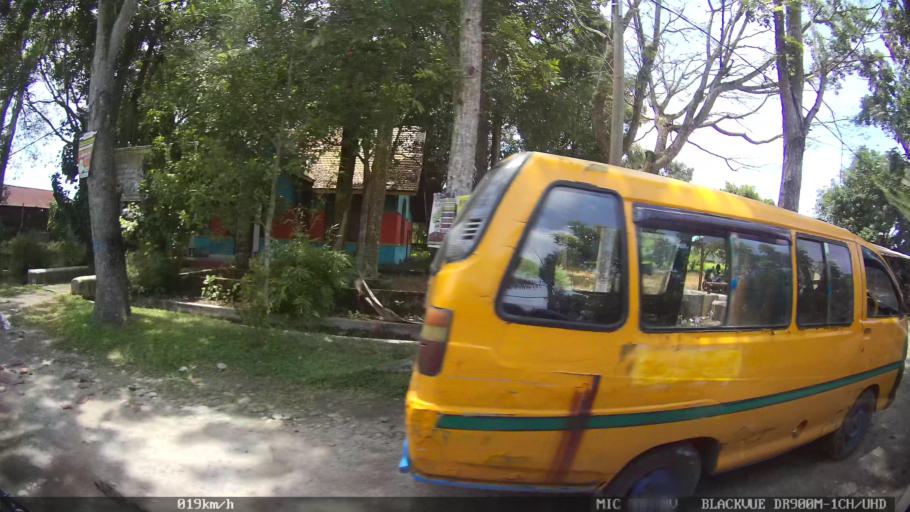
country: ID
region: North Sumatra
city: Perbaungan
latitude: 3.5412
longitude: 98.8803
